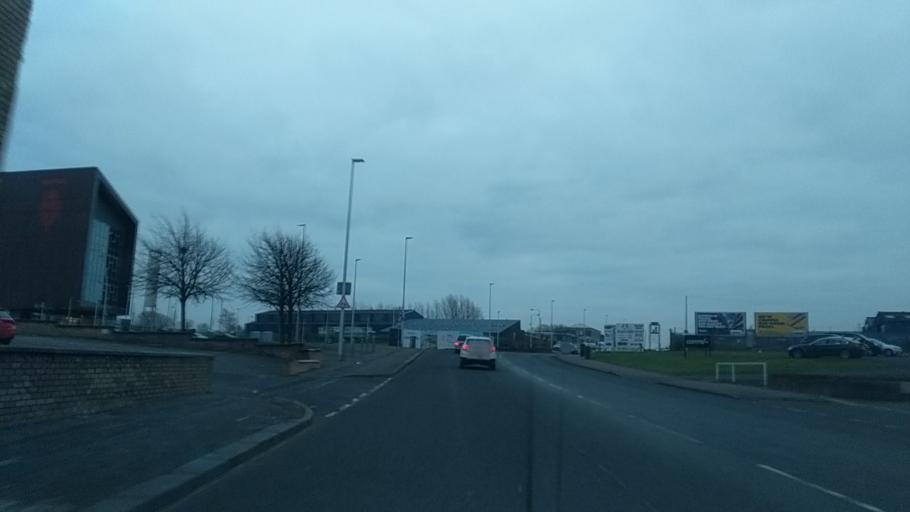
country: GB
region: Scotland
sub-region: South Lanarkshire
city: Rutherglen
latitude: 55.8369
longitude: -4.2282
